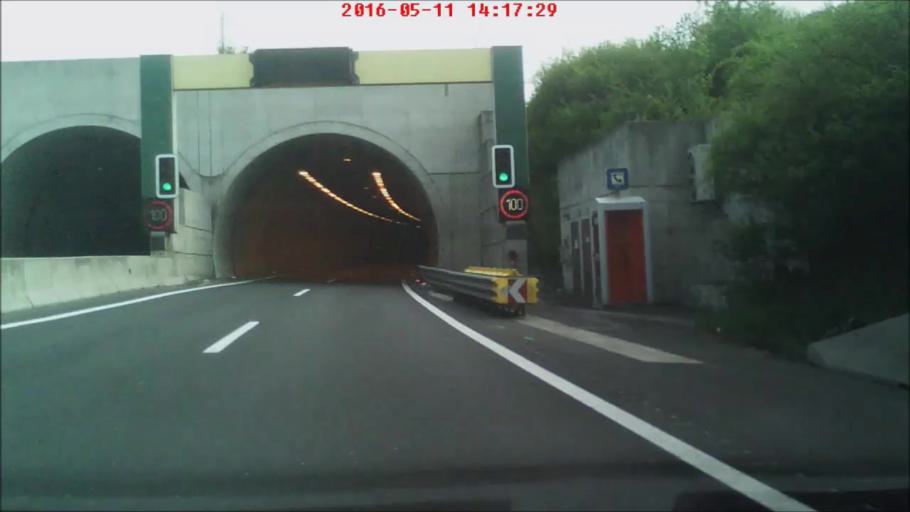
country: AT
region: Upper Austria
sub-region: Politischer Bezirk Kirchdorf an der Krems
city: Micheldorf in Oberoesterreich
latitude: 47.9236
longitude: 14.1013
